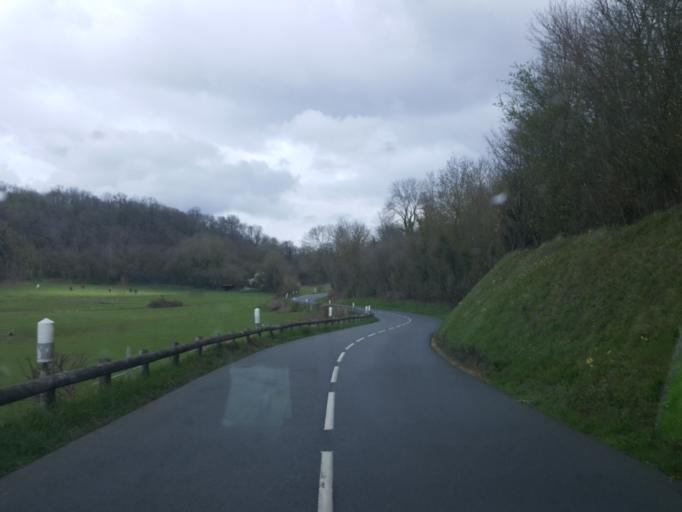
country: FR
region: Ile-de-France
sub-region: Departement du Val-d'Oise
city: Magny-en-Vexin
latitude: 49.1712
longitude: 1.7815
